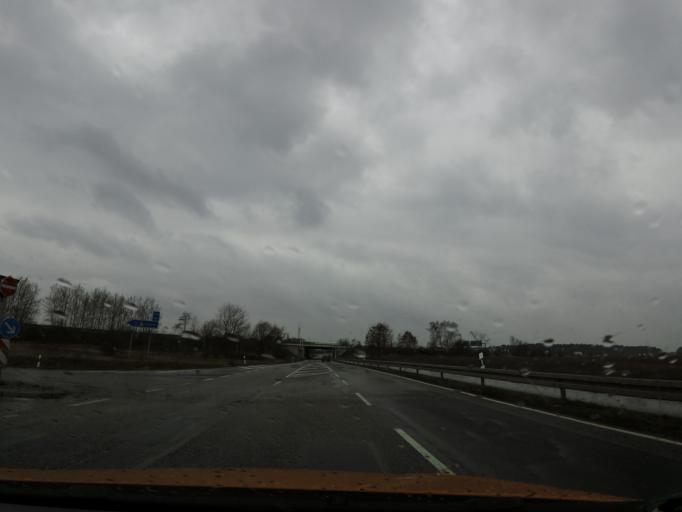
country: DE
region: Brandenburg
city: Ziesar
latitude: 52.2502
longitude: 12.2583
